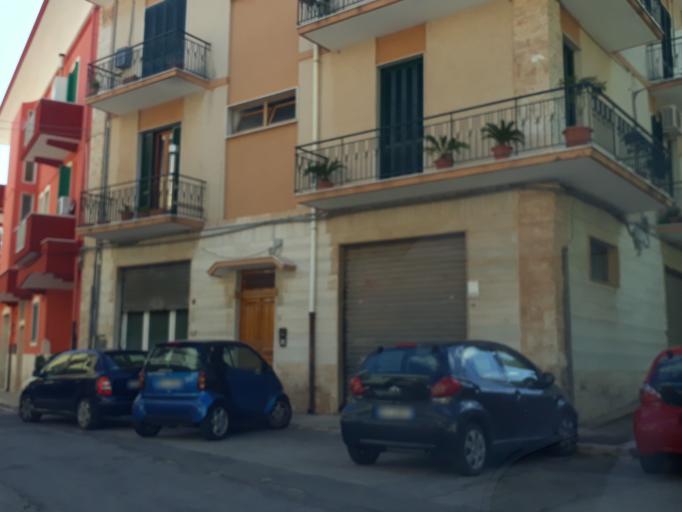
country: IT
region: Apulia
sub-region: Provincia di Brindisi
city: Fasano
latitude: 40.8321
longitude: 17.3531
